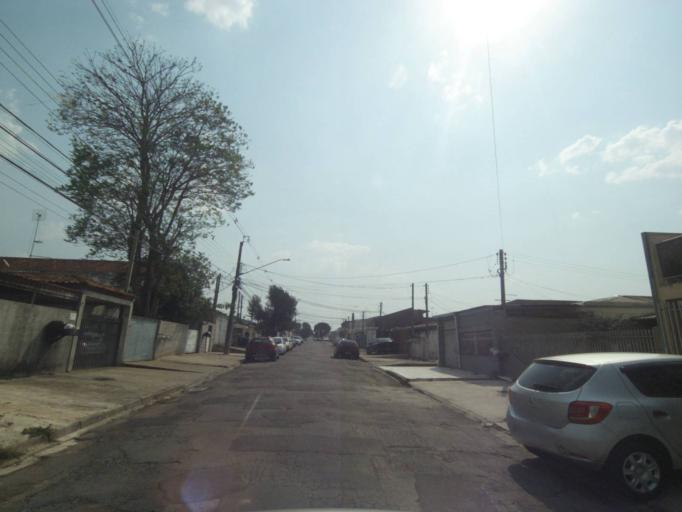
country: BR
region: Parana
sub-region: Sao Jose Dos Pinhais
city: Sao Jose dos Pinhais
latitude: -25.5385
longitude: -49.2372
